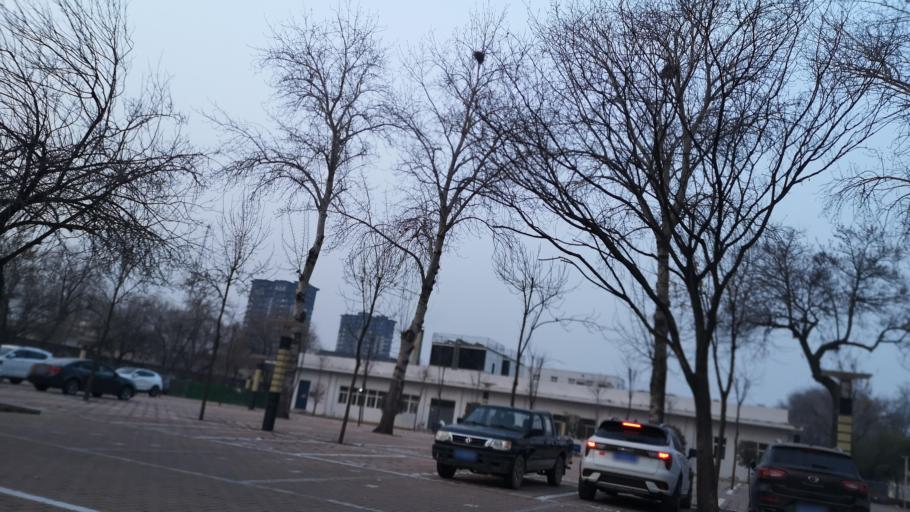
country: CN
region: Henan Sheng
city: Zhongyuanlu
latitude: 35.7786
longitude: 115.0745
